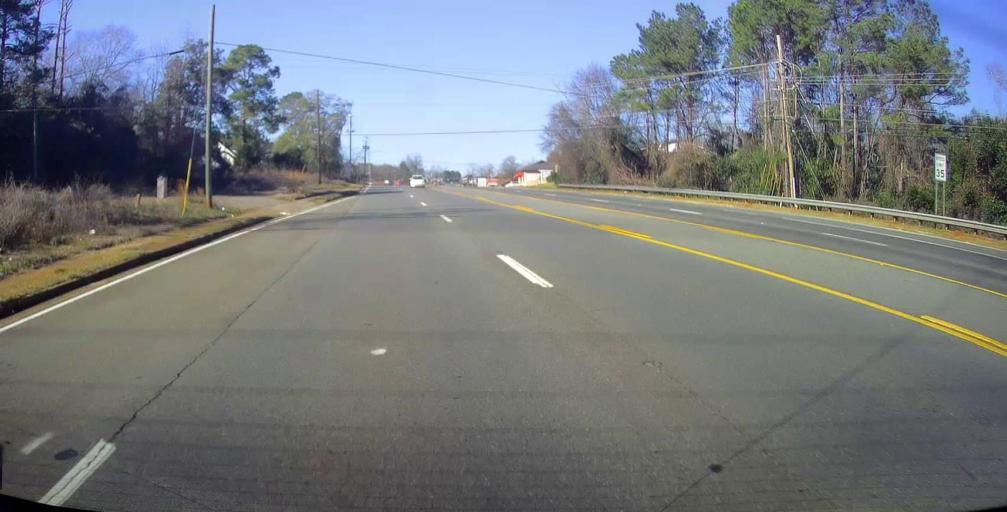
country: US
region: Georgia
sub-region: Sumter County
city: Americus
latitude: 32.0807
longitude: -84.2384
